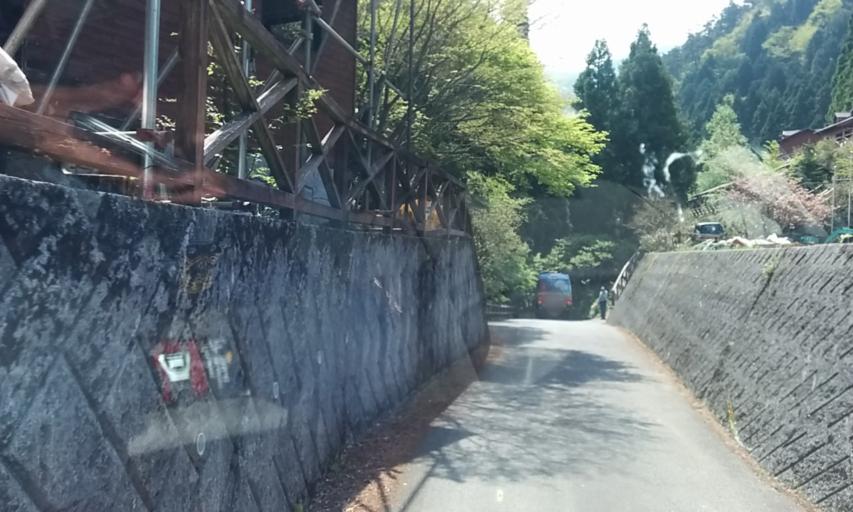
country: JP
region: Ehime
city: Niihama
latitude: 33.8782
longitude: 133.3113
